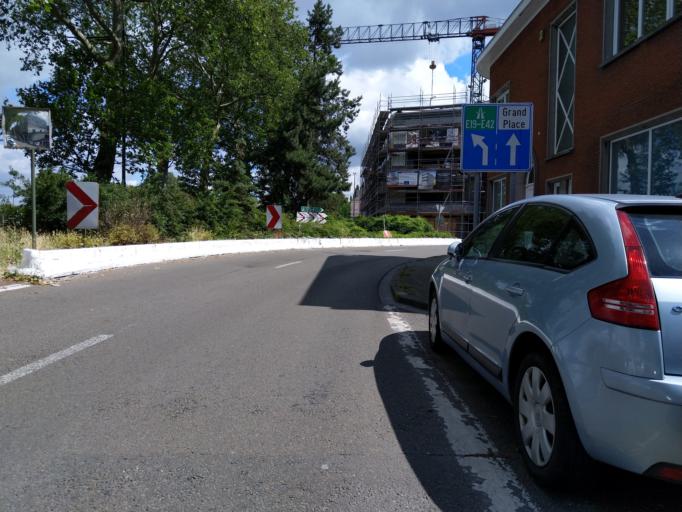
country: BE
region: Wallonia
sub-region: Province du Hainaut
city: Mons
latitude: 50.4579
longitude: 3.9475
